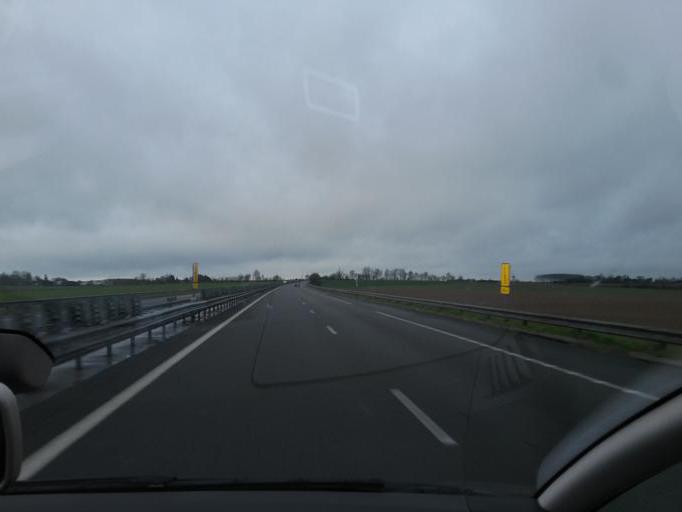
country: FR
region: Nord-Pas-de-Calais
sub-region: Departement du Pas-de-Calais
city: Hermies
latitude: 50.0822
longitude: 3.0317
